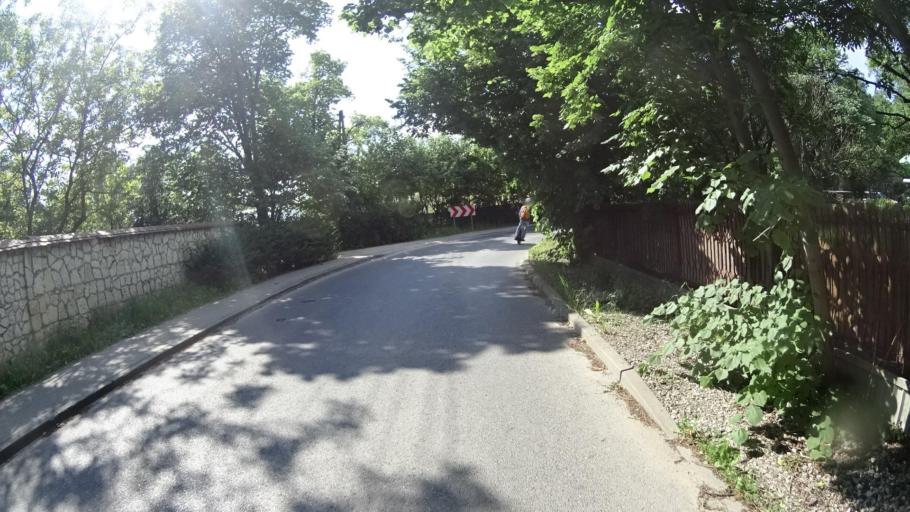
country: PL
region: Masovian Voivodeship
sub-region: Powiat piaseczynski
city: Mysiadlo
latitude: 52.1144
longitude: 21.0283
